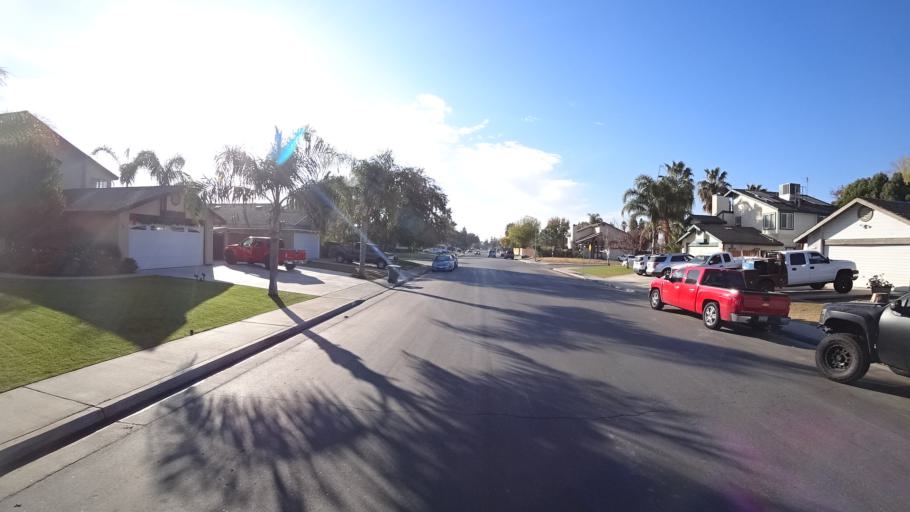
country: US
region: California
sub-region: Kern County
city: Rosedale
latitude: 35.3530
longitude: -119.1483
